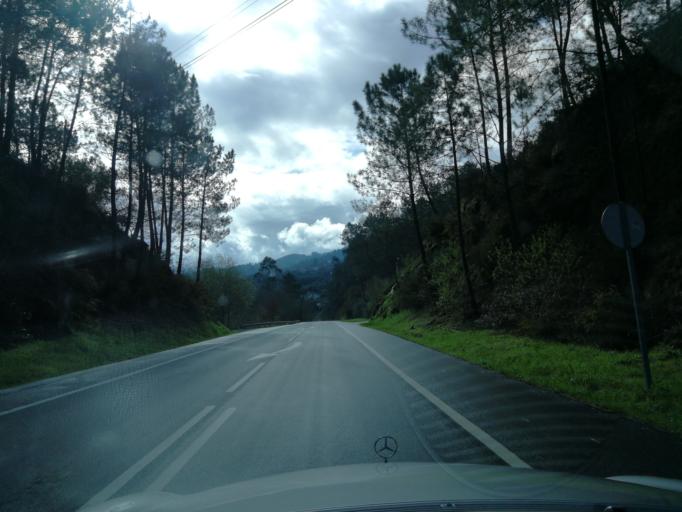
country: PT
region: Viana do Castelo
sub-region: Ponte da Barca
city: Ponte da Barca
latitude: 41.8094
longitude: -8.3739
